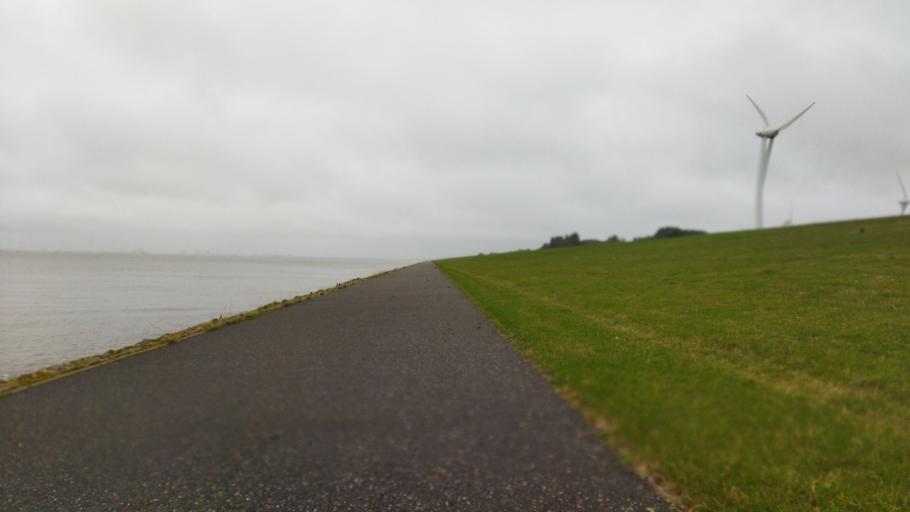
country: DE
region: Lower Saxony
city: Emden
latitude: 53.3348
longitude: 7.0863
